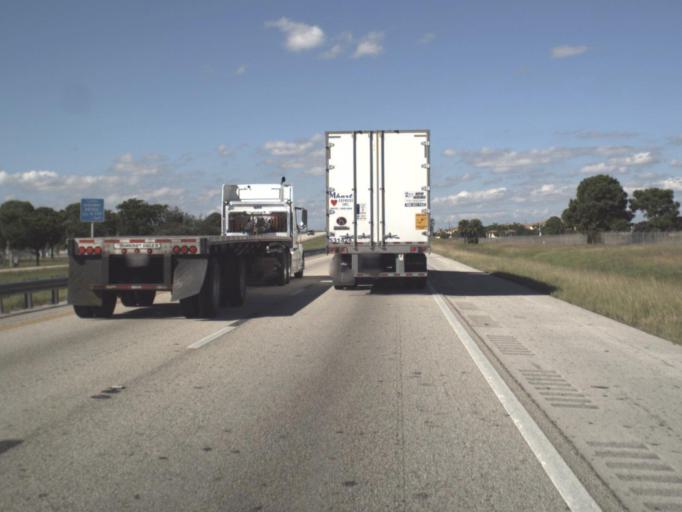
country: US
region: Florida
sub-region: Miami-Dade County
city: Lake Lucerne
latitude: 25.9722
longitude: -80.2571
